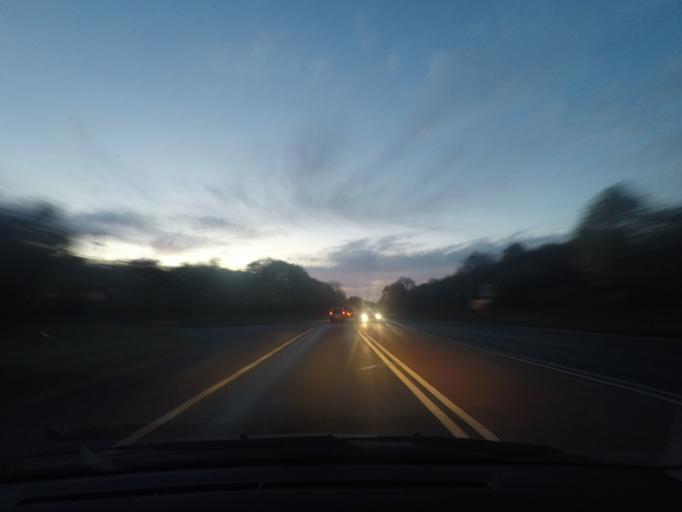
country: GB
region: England
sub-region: East Riding of Yorkshire
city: Wilberfoss
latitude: 53.9481
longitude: -0.8978
